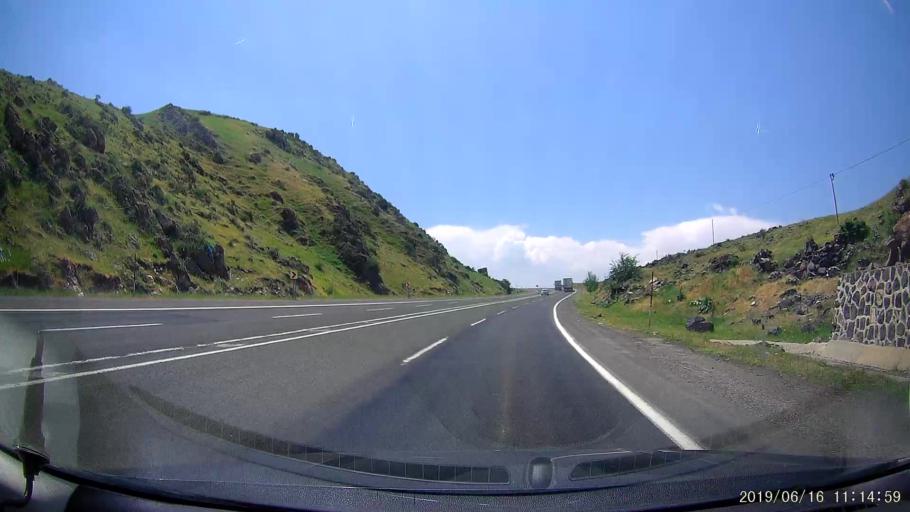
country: TR
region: Igdir
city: Igdir
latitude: 39.7707
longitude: 44.1435
